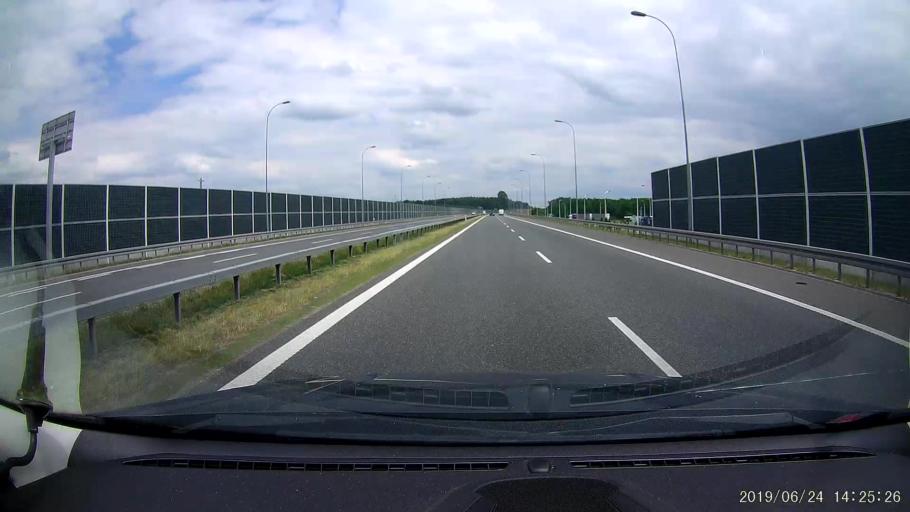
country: PL
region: Lesser Poland Voivodeship
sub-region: Powiat brzeski
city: Brzesko
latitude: 49.9984
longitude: 20.6200
